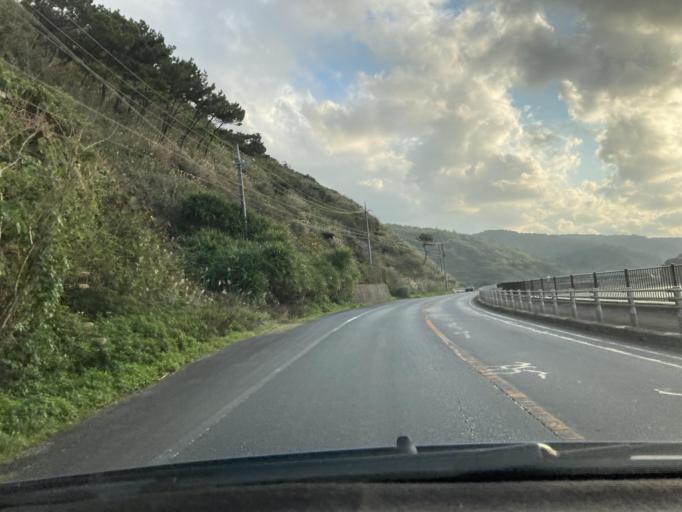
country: JP
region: Okinawa
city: Nago
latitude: 26.7923
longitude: 128.2250
